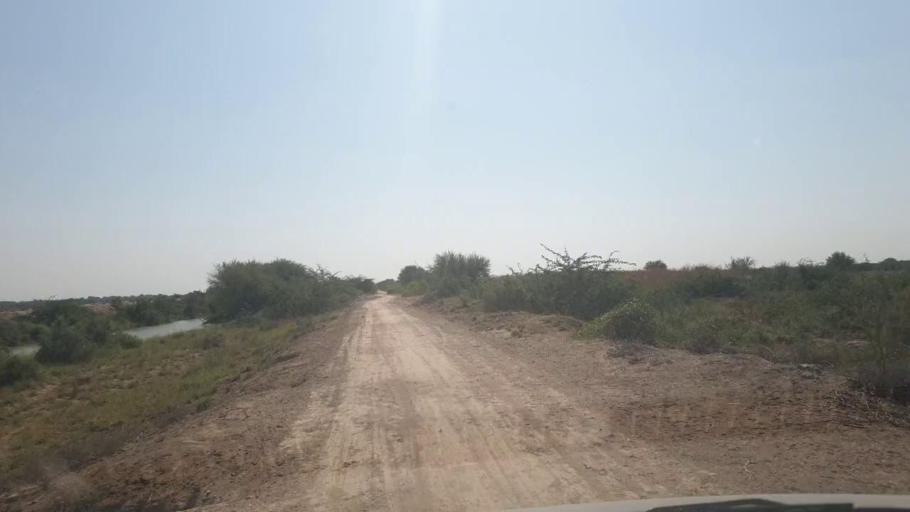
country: PK
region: Sindh
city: Tando Bago
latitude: 24.9120
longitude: 69.1645
